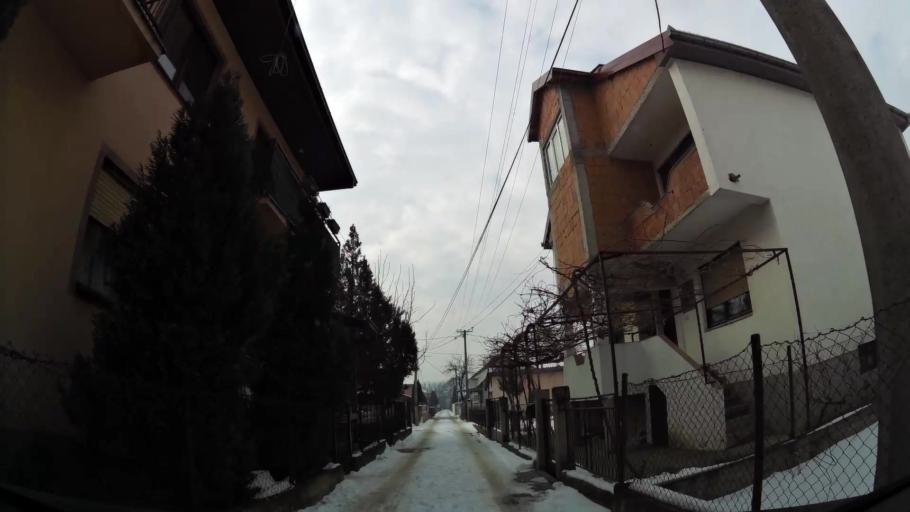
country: MK
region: Saraj
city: Saraj
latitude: 42.0258
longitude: 21.3553
